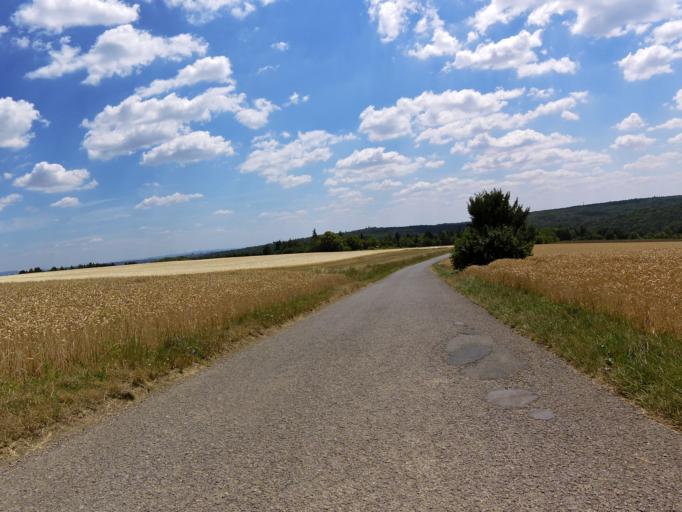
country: DE
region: Bavaria
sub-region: Regierungsbezirk Unterfranken
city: Hochberg
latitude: 49.7774
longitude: 9.8886
